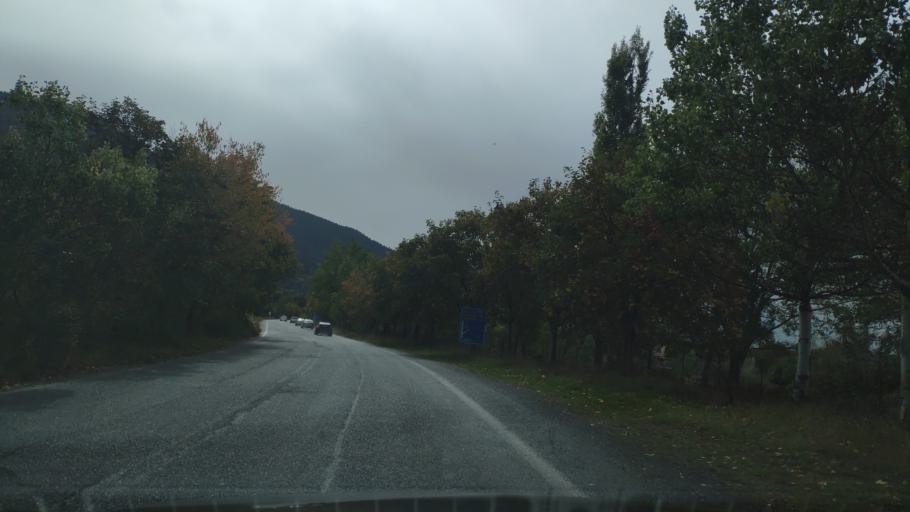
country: GR
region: Peloponnese
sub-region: Nomos Arkadias
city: Langadhia
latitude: 37.6772
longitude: 22.1912
